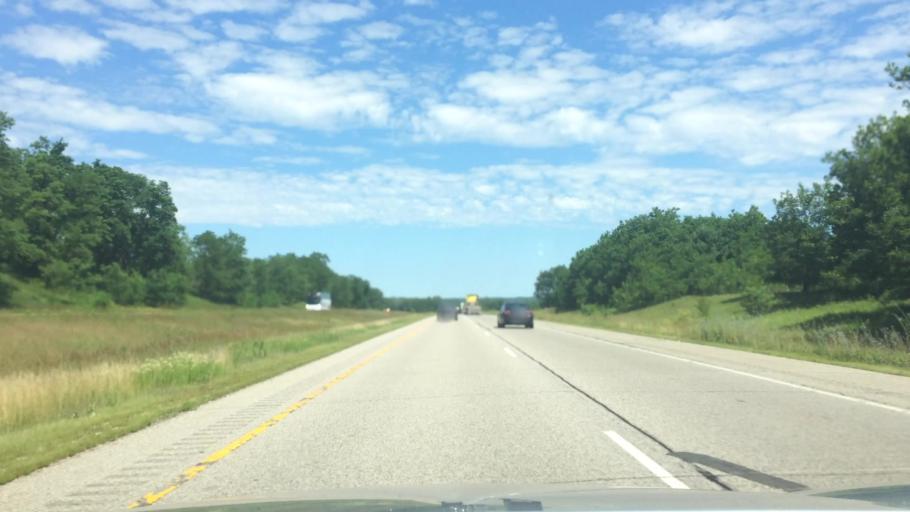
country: US
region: Wisconsin
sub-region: Marquette County
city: Westfield
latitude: 43.7261
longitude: -89.4817
